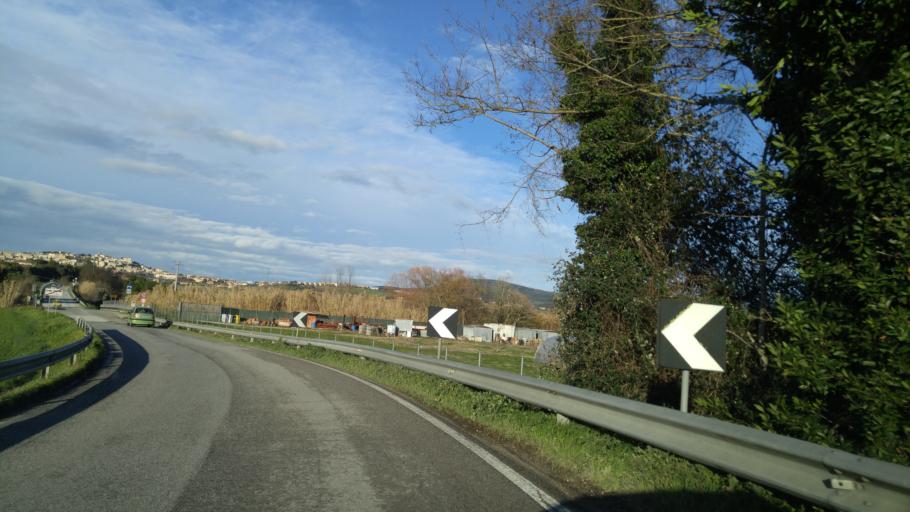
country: IT
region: The Marches
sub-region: Provincia di Ancona
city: Camerano
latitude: 43.5023
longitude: 13.5457
